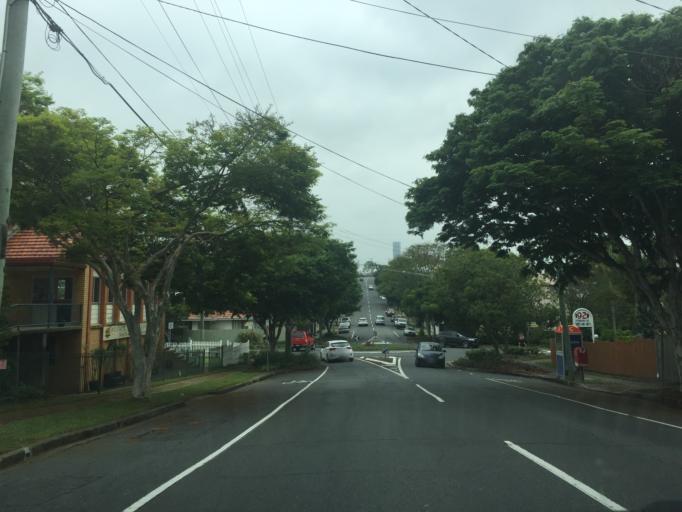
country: AU
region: Queensland
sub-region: Brisbane
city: Milton
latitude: -27.4631
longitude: 152.9960
